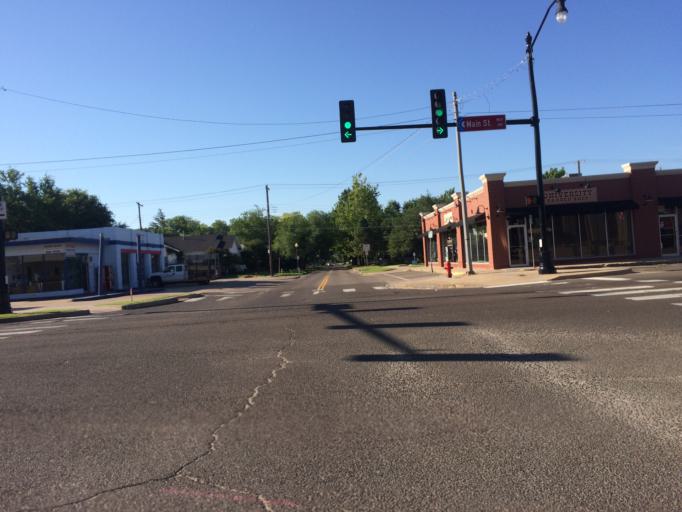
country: US
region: Oklahoma
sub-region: Cleveland County
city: Norman
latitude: 35.2191
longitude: -97.4482
